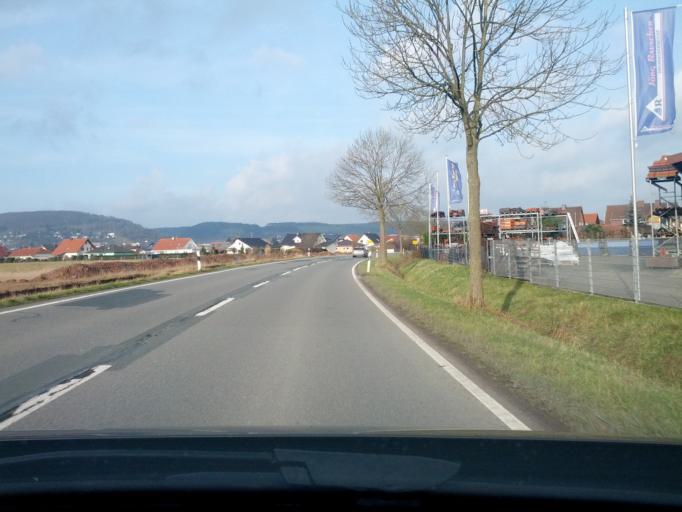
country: DE
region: North Rhine-Westphalia
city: Beverungen
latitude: 51.6532
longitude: 9.3877
